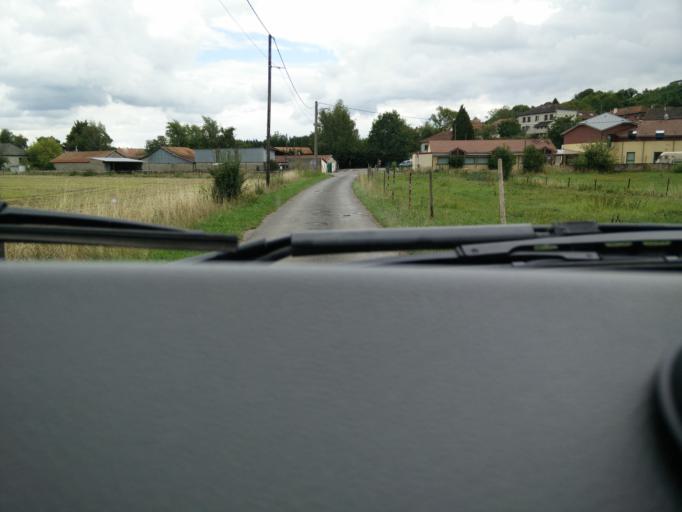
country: FR
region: Lorraine
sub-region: Departement de la Meuse
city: Stenay
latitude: 49.3900
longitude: 5.1806
